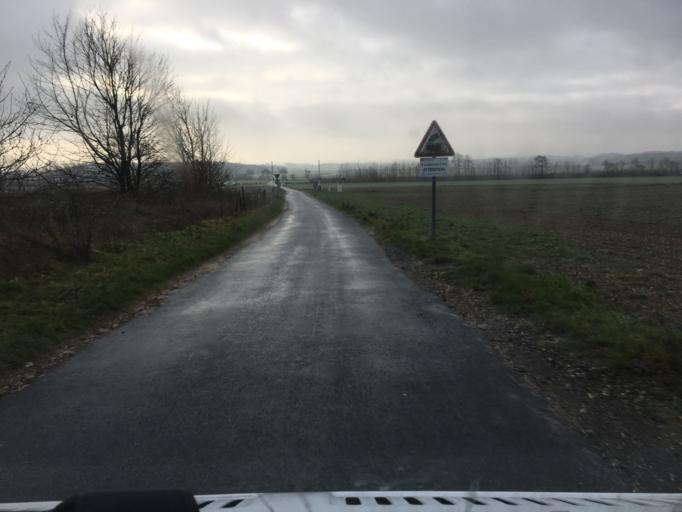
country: FR
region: Picardie
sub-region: Departement de la Somme
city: Saint-Valery-sur-Somme
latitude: 50.1770
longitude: 1.6205
